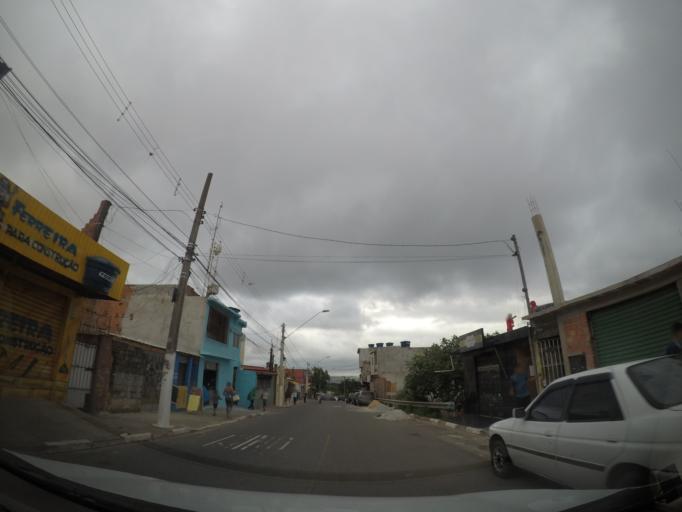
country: BR
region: Sao Paulo
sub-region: Aruja
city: Aruja
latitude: -23.3991
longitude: -46.4220
